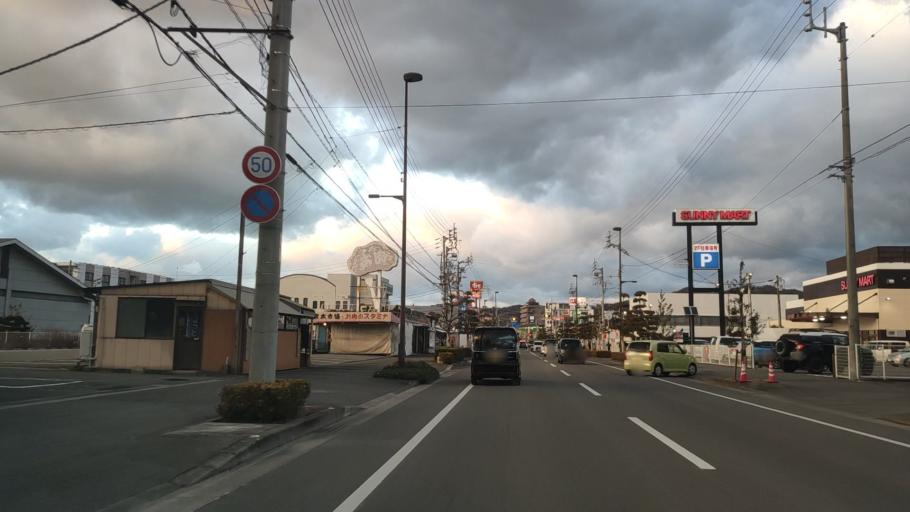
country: JP
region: Ehime
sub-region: Shikoku-chuo Shi
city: Matsuyama
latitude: 33.8346
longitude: 132.7871
